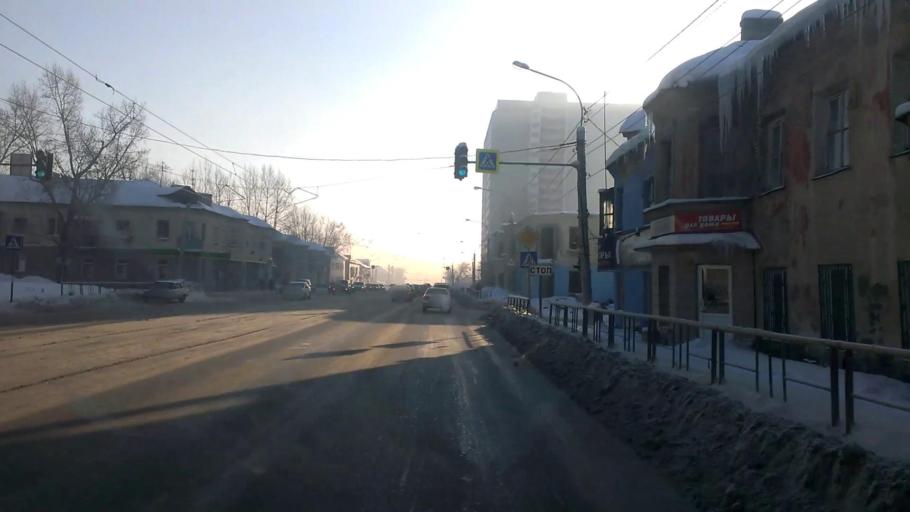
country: RU
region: Altai Krai
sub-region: Gorod Barnaulskiy
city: Barnaul
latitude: 53.3471
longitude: 83.7311
